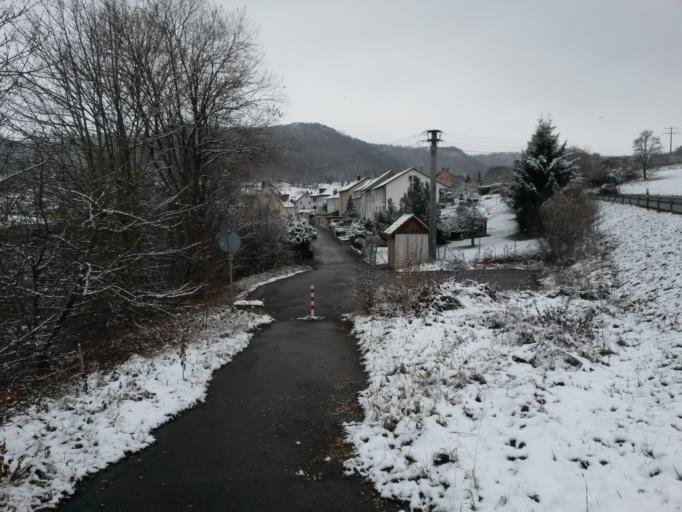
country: DE
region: Baden-Wuerttemberg
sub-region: Regierungsbezirk Stuttgart
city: Bad Uberkingen
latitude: 48.6050
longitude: 9.7972
